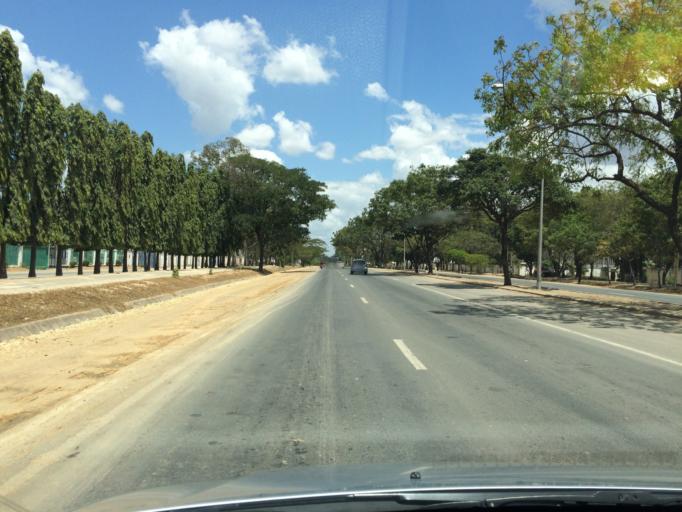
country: TZ
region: Dar es Salaam
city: Dar es Salaam
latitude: -6.8415
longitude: 39.2510
